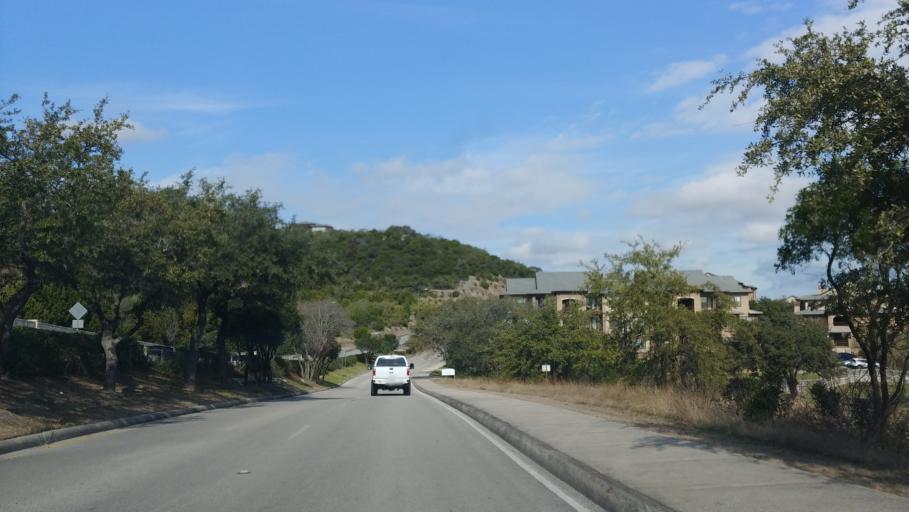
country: US
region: Texas
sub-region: Bexar County
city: Cross Mountain
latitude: 29.6204
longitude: -98.6116
